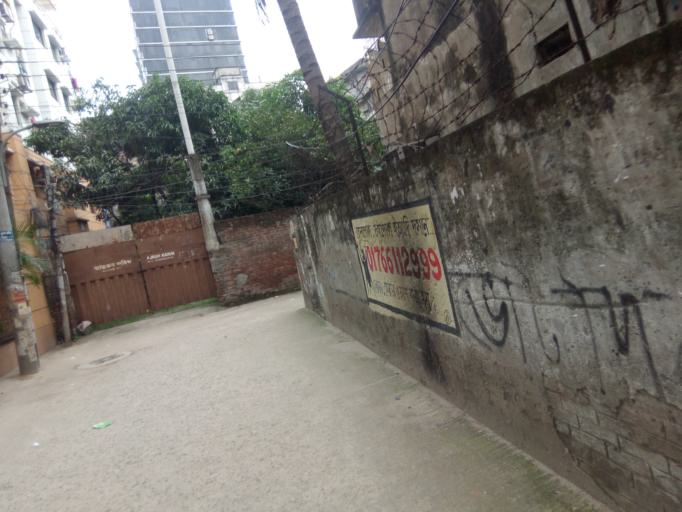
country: BD
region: Dhaka
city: Paltan
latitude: 23.7381
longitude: 90.4129
